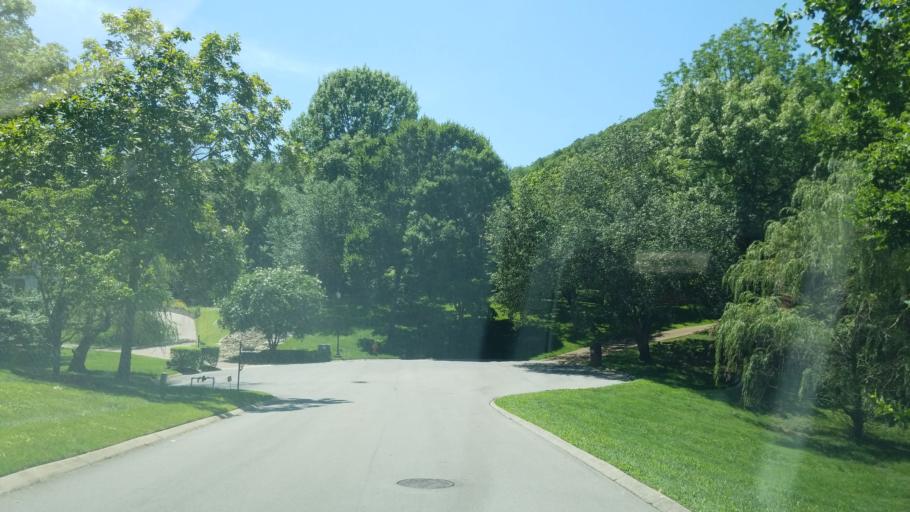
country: US
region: Tennessee
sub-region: Davidson County
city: Forest Hills
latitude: 36.0563
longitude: -86.8199
